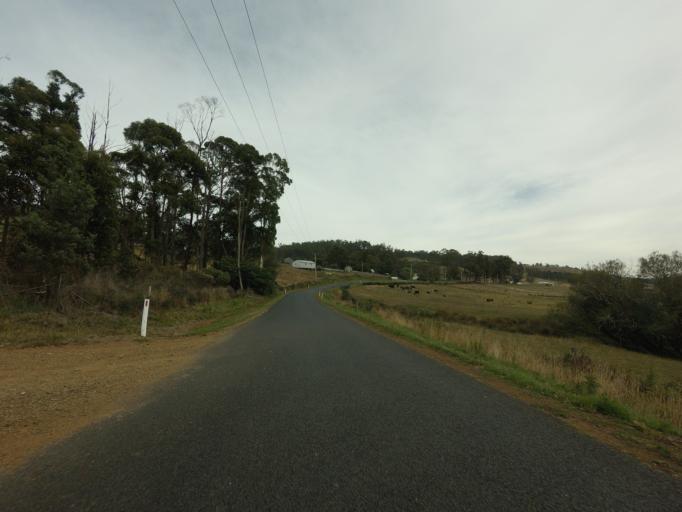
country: AU
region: Tasmania
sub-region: Sorell
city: Sorell
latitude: -42.4692
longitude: 147.5690
